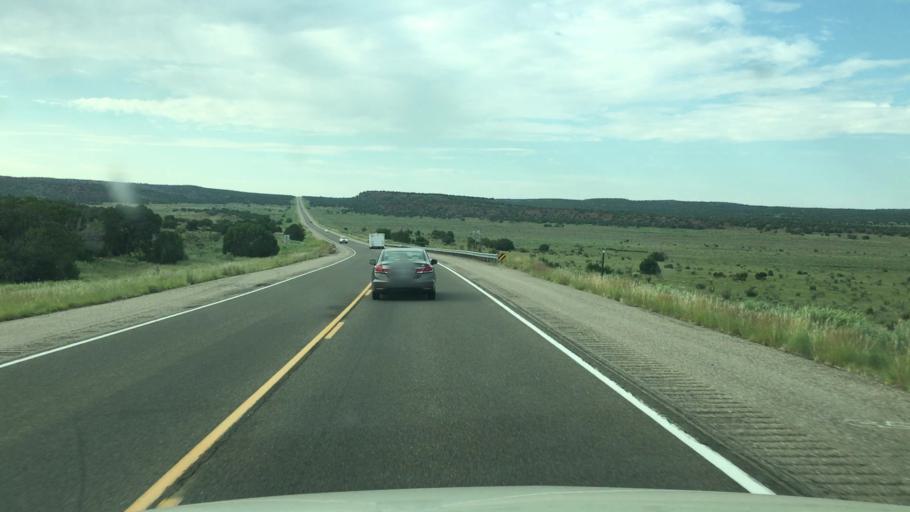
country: US
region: New Mexico
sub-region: Santa Fe County
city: Eldorado at Santa Fe
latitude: 35.2556
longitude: -105.8086
